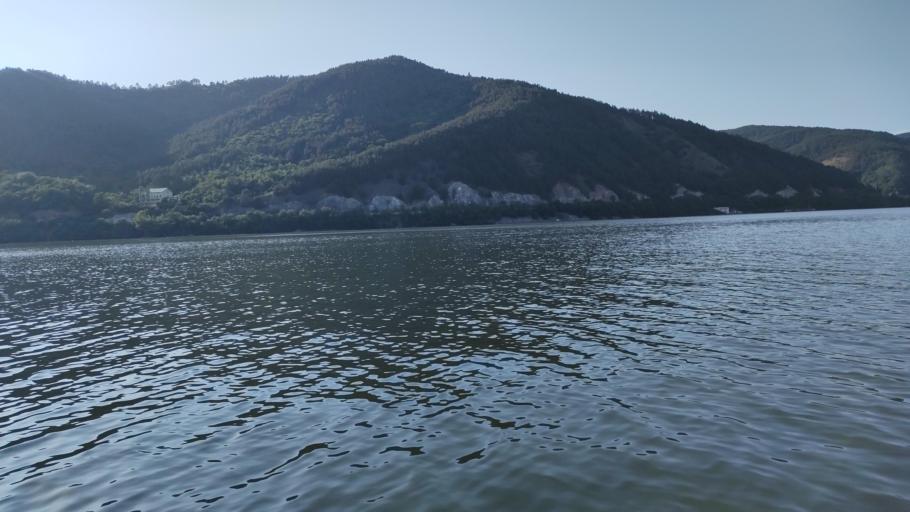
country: RO
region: Mehedinti
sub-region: Comuna Svinita
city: Svinita
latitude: 44.5179
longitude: 22.2028
